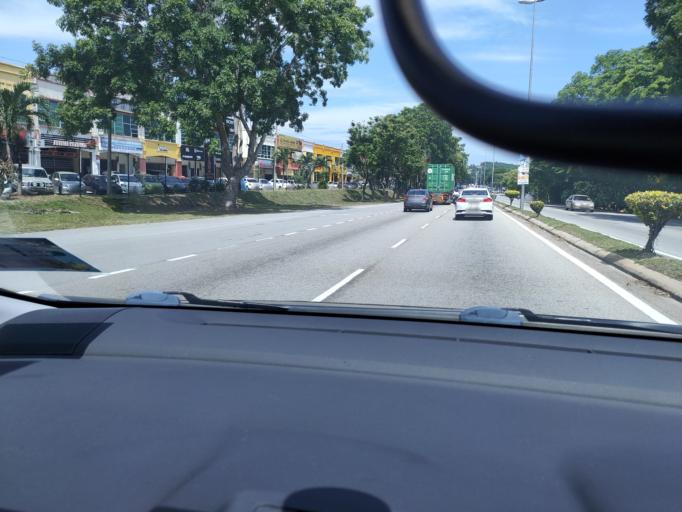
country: MY
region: Melaka
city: Bukit Rambai
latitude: 2.2726
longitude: 102.2163
